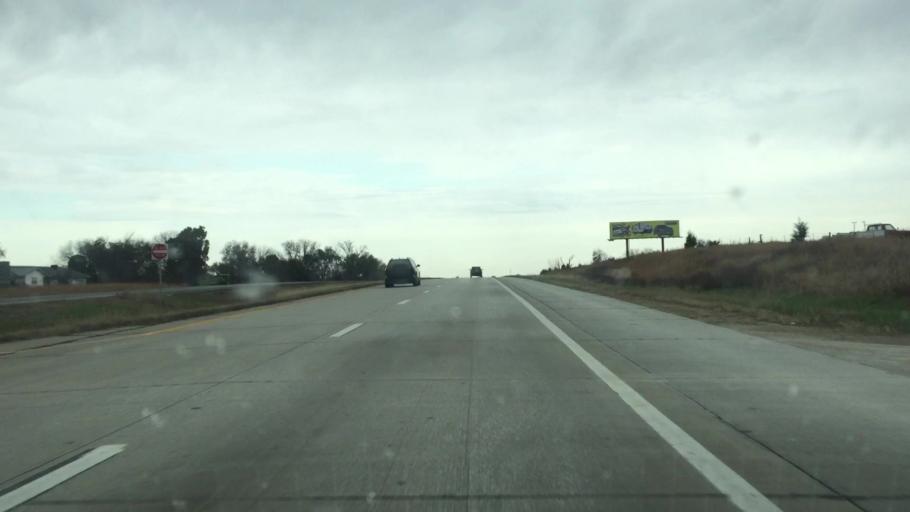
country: US
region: Missouri
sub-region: Saint Clair County
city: Osceola
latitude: 38.1662
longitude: -93.7220
